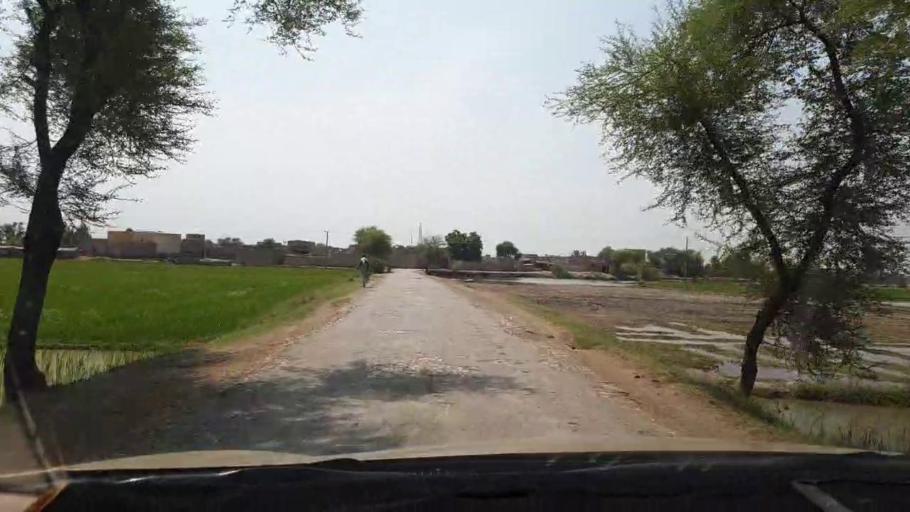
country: PK
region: Sindh
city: Naudero
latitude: 27.6345
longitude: 68.2743
